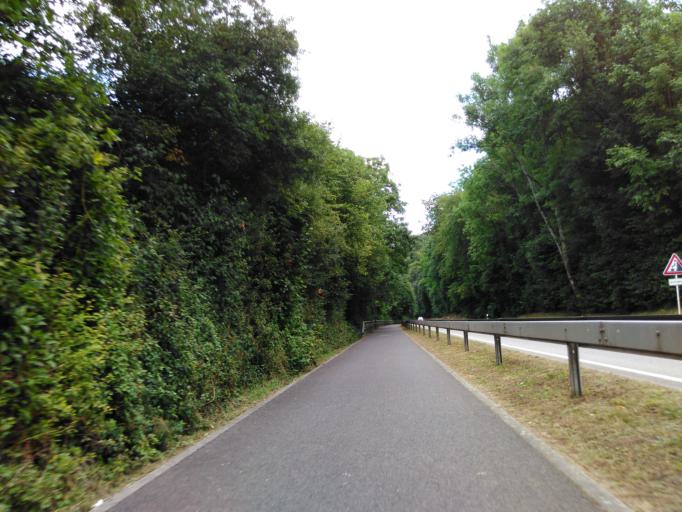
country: DE
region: Rheinland-Pfalz
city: Ralingen
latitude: 49.8134
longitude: 6.4842
